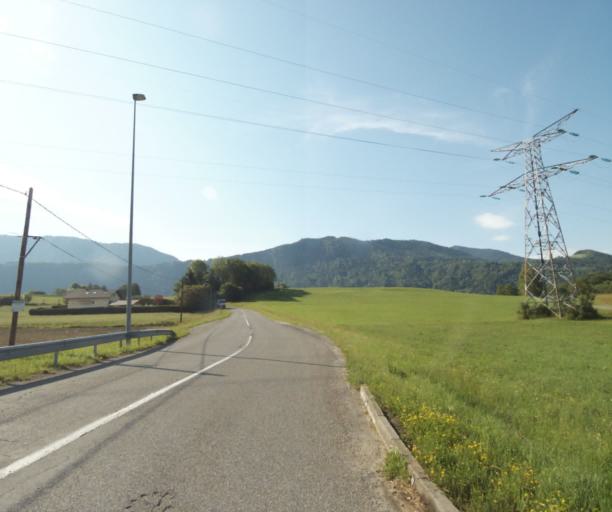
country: FR
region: Rhone-Alpes
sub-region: Departement de la Haute-Savoie
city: Allinges
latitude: 46.3203
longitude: 6.4754
